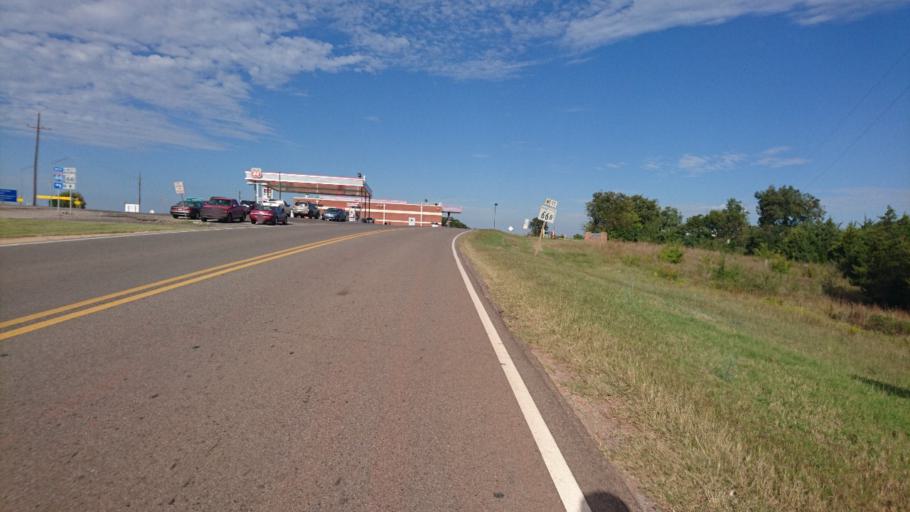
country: US
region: Oklahoma
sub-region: Oklahoma County
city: Luther
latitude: 35.6812
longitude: -97.0532
